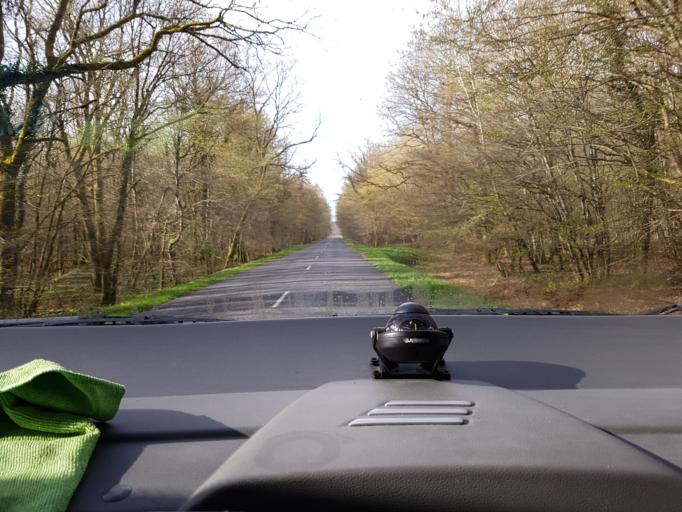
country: FR
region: Bourgogne
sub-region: Departement de Saone-et-Loire
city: Etang-sur-Arroux
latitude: 46.7972
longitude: 4.1513
